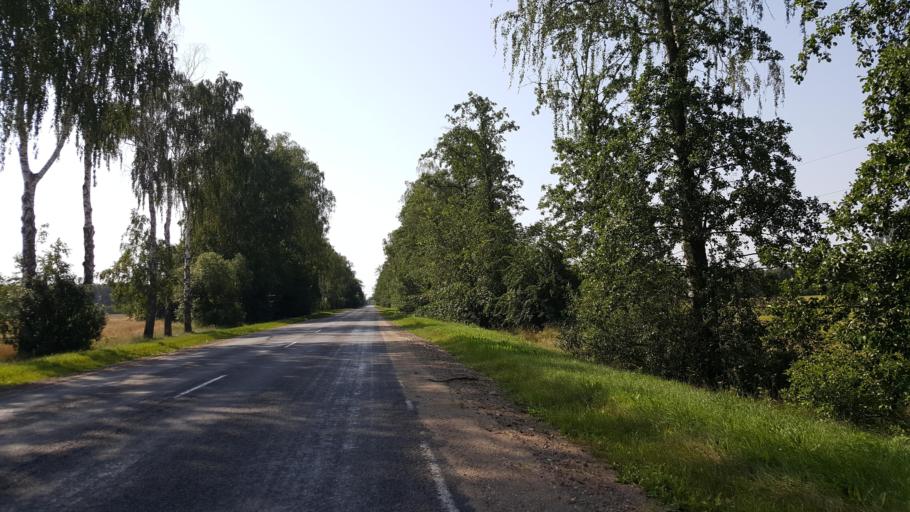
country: BY
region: Brest
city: Zhabinka
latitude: 52.2469
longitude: 23.9725
